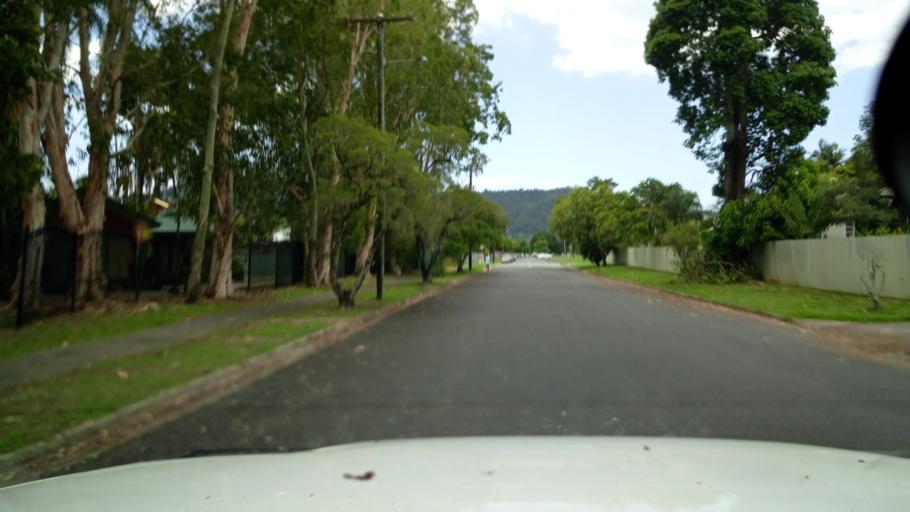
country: AU
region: Queensland
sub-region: Cairns
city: Cairns
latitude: -16.9173
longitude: 145.7406
